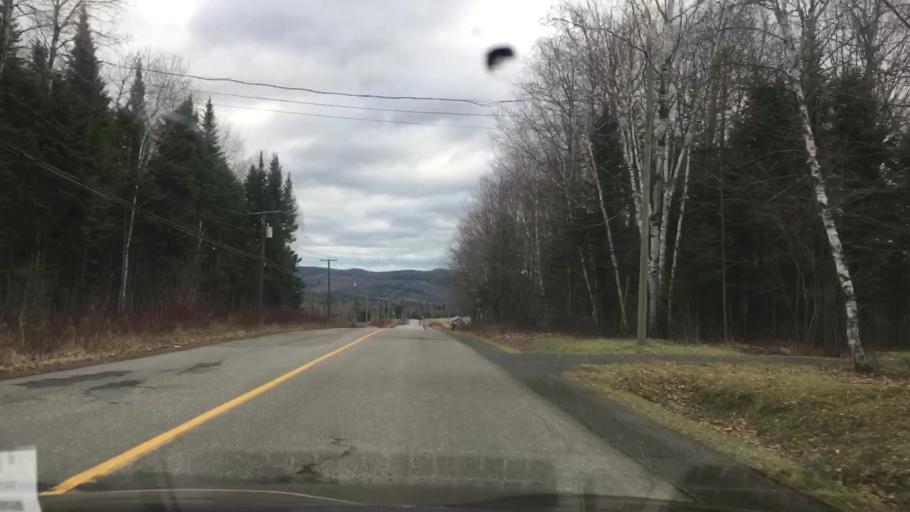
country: US
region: Maine
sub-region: Aroostook County
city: Fort Fairfield
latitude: 46.7481
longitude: -67.7441
